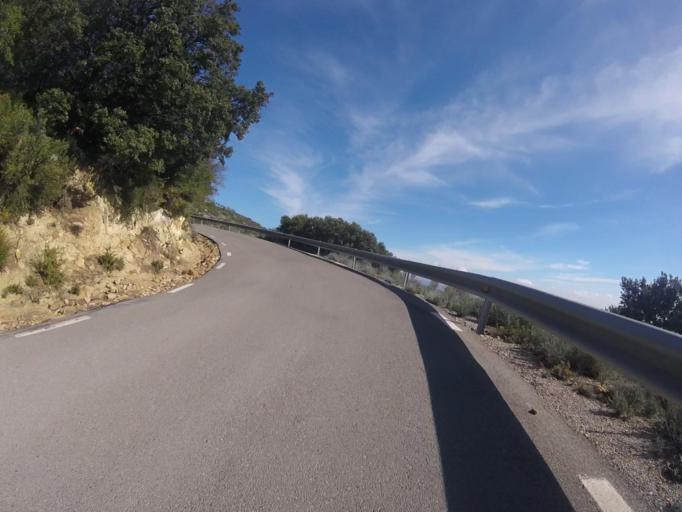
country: ES
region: Valencia
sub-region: Provincia de Castello
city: Sarratella
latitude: 40.2904
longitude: 0.0337
